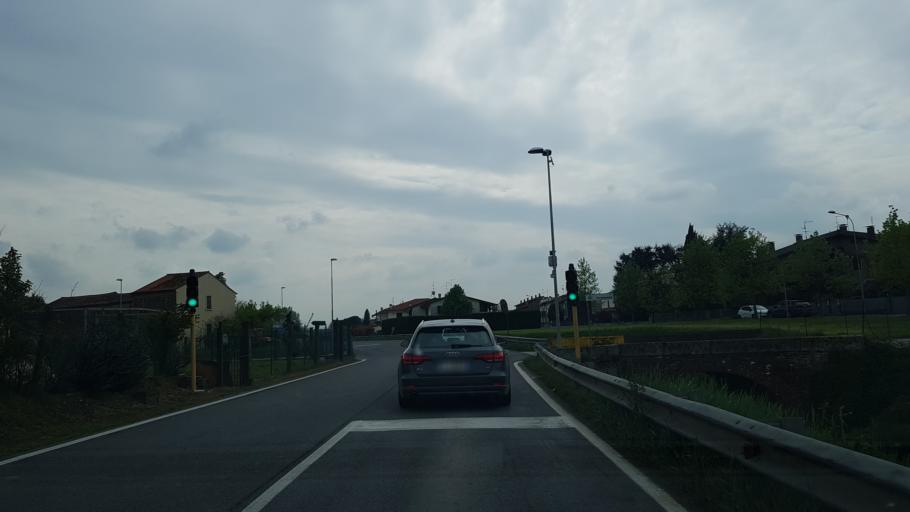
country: IT
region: Veneto
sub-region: Provincia di Verona
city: Albaredo d'Adige
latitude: 45.3148
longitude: 11.2783
